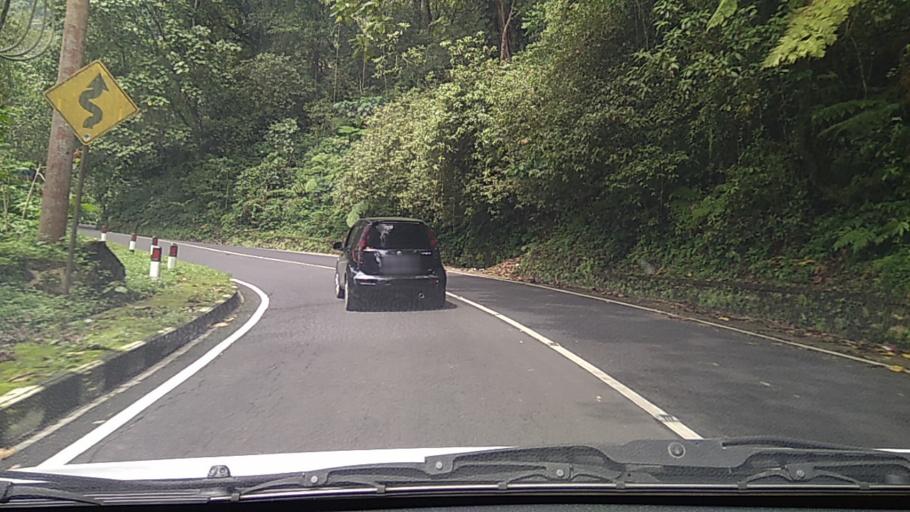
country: ID
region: Bali
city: Munduk
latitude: -8.2406
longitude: 115.1446
